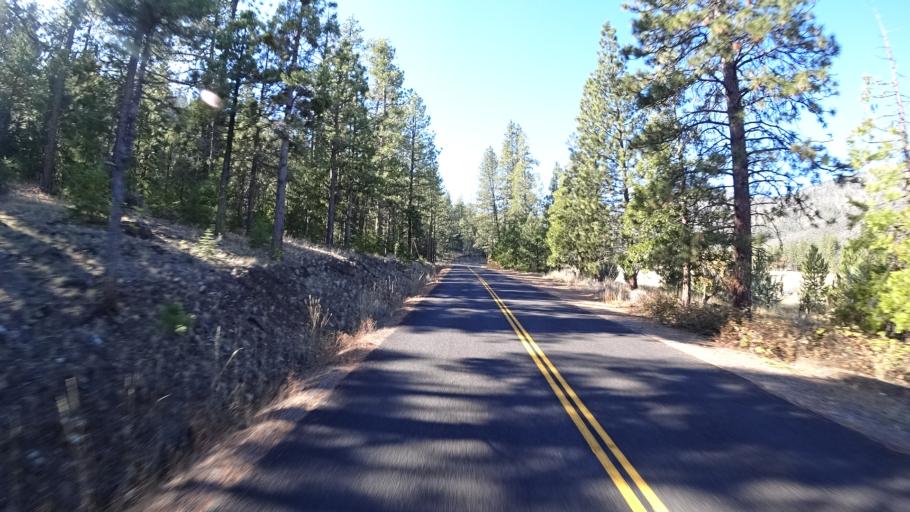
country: US
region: California
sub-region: Siskiyou County
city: Weed
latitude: 41.4327
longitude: -122.4831
